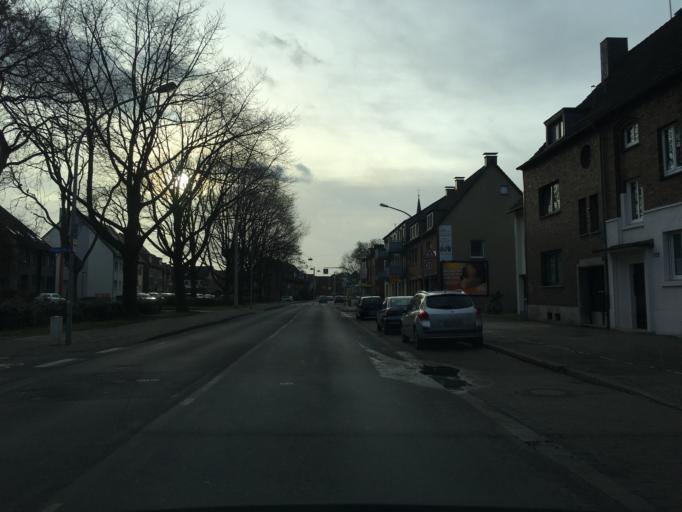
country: DE
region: North Rhine-Westphalia
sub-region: Regierungsbezirk Dusseldorf
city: Dinslaken
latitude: 51.5271
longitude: 6.7926
